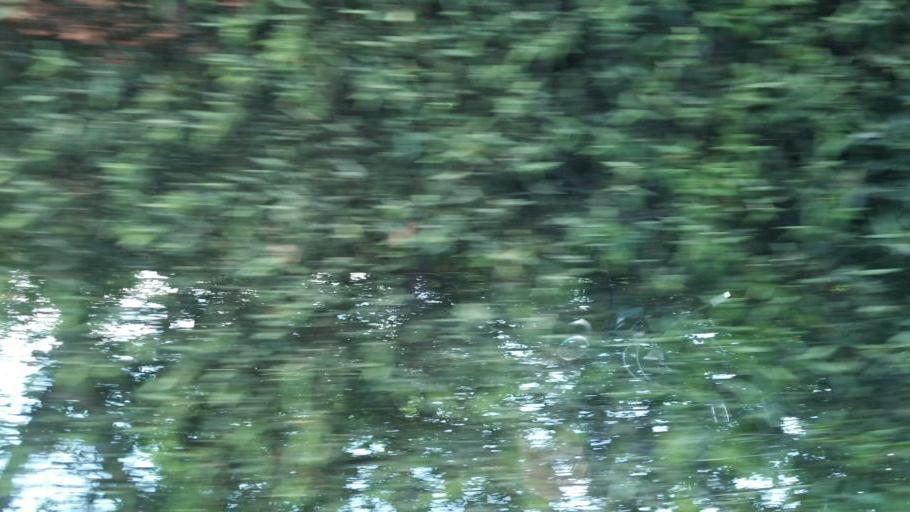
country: US
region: Arizona
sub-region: Maricopa County
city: Phoenix
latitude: 33.5469
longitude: -112.0629
